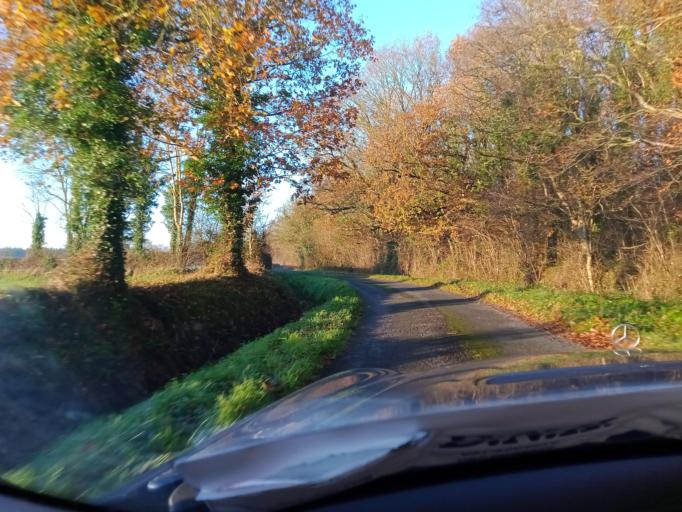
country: IE
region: Leinster
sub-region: Kilkenny
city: Callan
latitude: 52.5292
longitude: -7.4536
